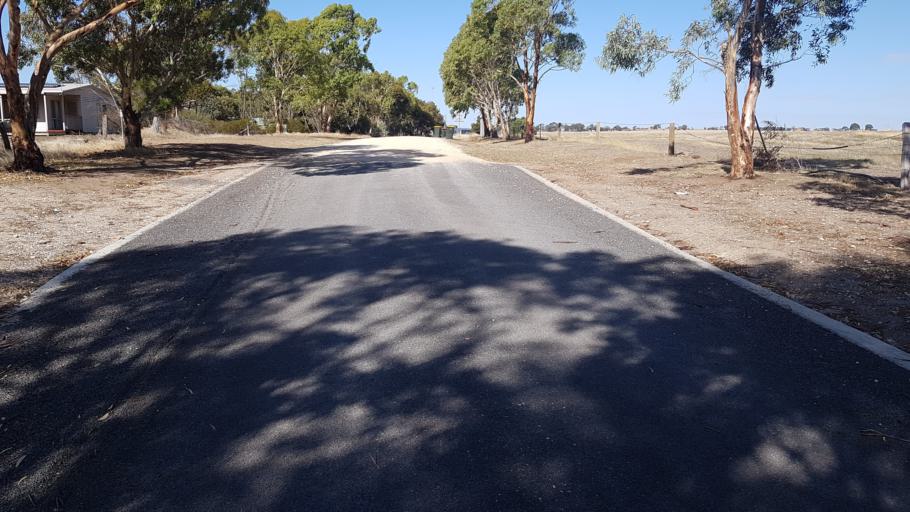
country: AU
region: Victoria
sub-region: Horsham
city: Horsham
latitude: -36.7434
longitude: 141.9434
